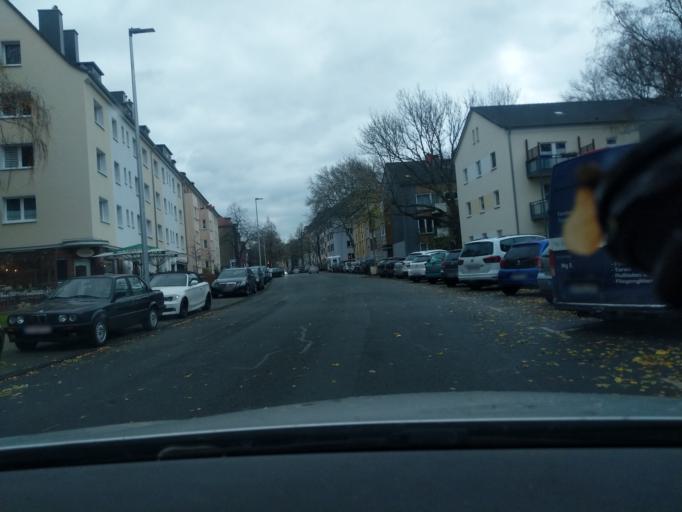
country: DE
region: North Rhine-Westphalia
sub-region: Regierungsbezirk Arnsberg
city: Dortmund
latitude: 51.5052
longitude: 7.4476
